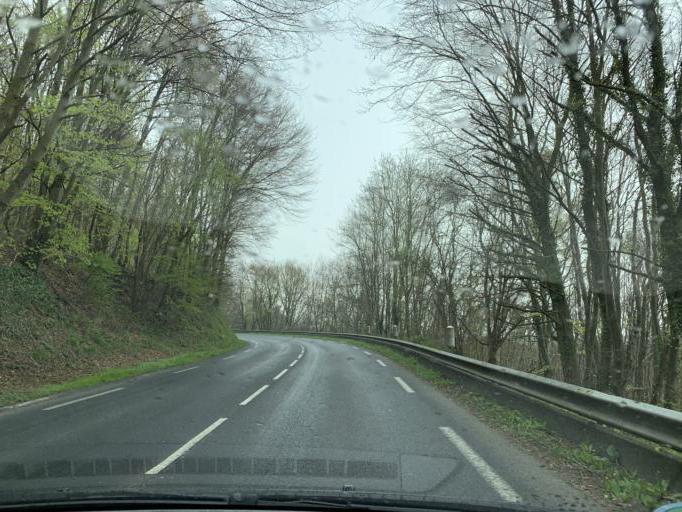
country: FR
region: Haute-Normandie
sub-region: Departement de la Seine-Maritime
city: Cany-Barville
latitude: 49.7853
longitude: 0.6485
